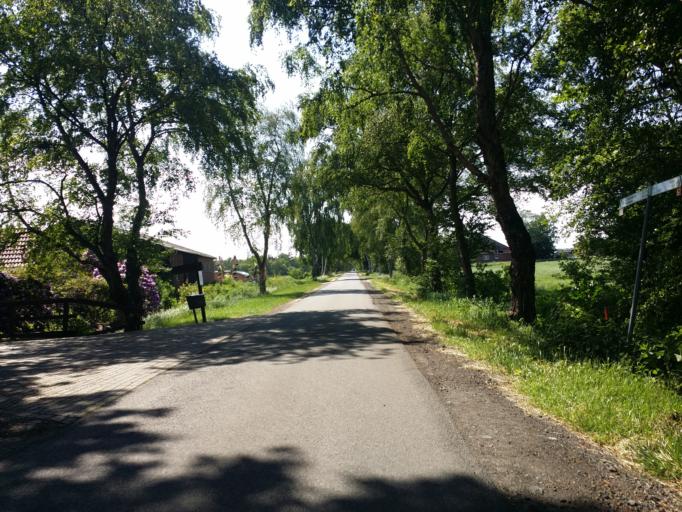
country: DE
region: Lower Saxony
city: Oldenburg
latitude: 53.2058
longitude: 8.3271
